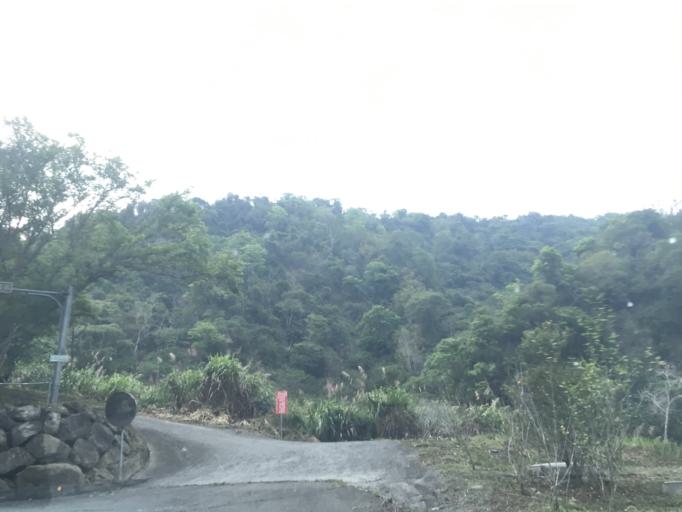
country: TW
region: Taiwan
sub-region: Nantou
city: Puli
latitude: 23.9522
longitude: 120.8571
